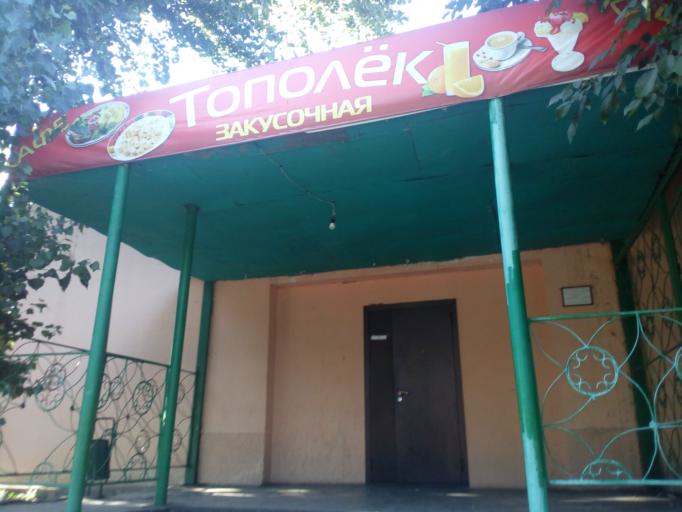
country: RU
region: Rostov
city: Sholokhovskiy
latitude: 48.2793
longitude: 41.0426
